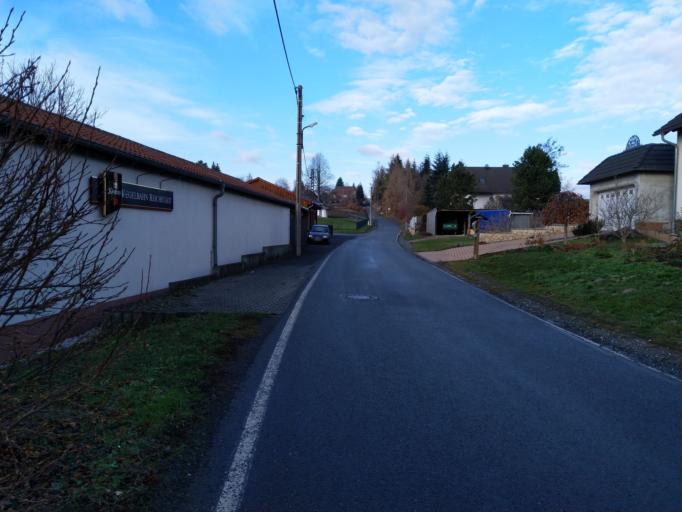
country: DE
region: Thuringia
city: Lobichau
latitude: 50.9204
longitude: 12.2375
